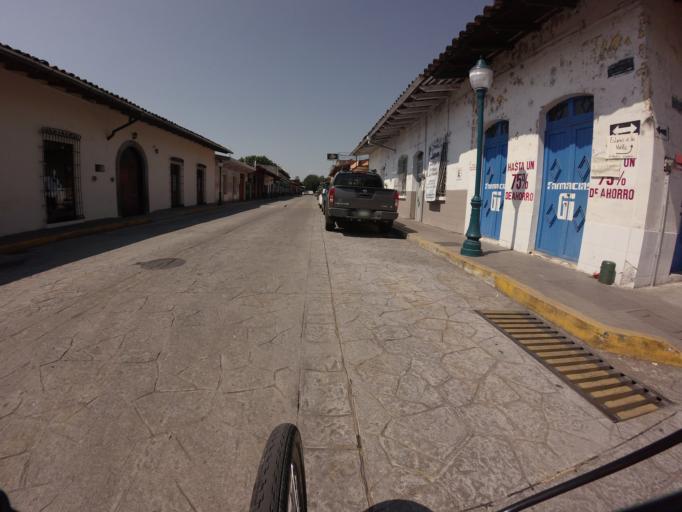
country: MX
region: Veracruz
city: Coatepec
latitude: 19.4567
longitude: -96.9576
